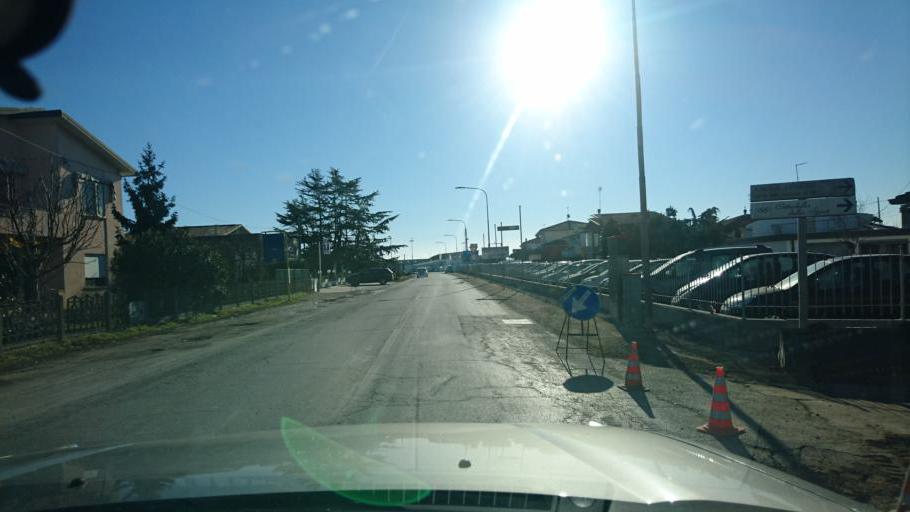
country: IT
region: Veneto
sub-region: Provincia di Rovigo
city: Porto Viro
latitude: 45.0329
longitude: 12.2322
